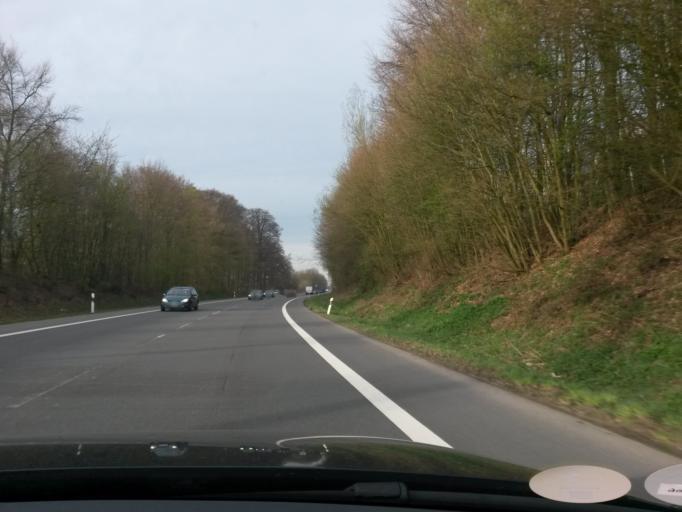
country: DE
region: North Rhine-Westphalia
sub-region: Regierungsbezirk Arnsberg
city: Luedenscheid
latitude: 51.2524
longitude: 7.6011
